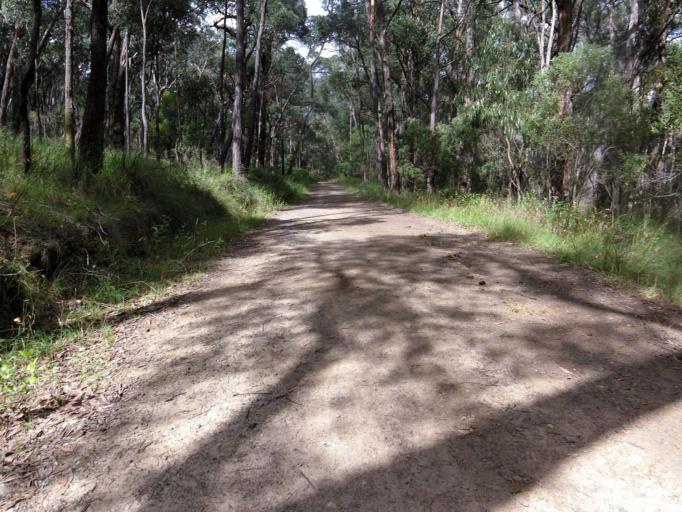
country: AU
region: Victoria
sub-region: Knox
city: The Basin
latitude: -37.8401
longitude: 145.3341
